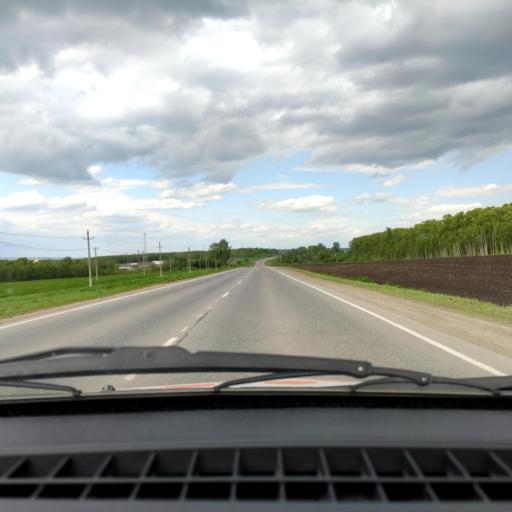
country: RU
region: Bashkortostan
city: Iglino
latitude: 54.8766
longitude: 56.4697
